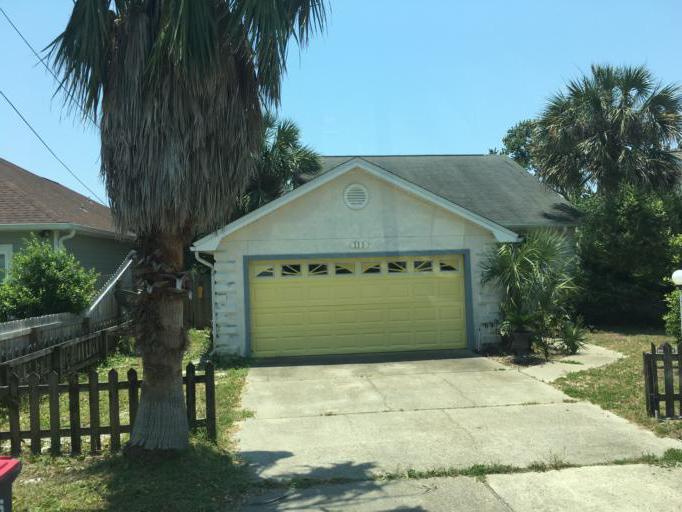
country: US
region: Florida
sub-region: Bay County
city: Panama City Beach
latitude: 30.2125
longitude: -85.8555
